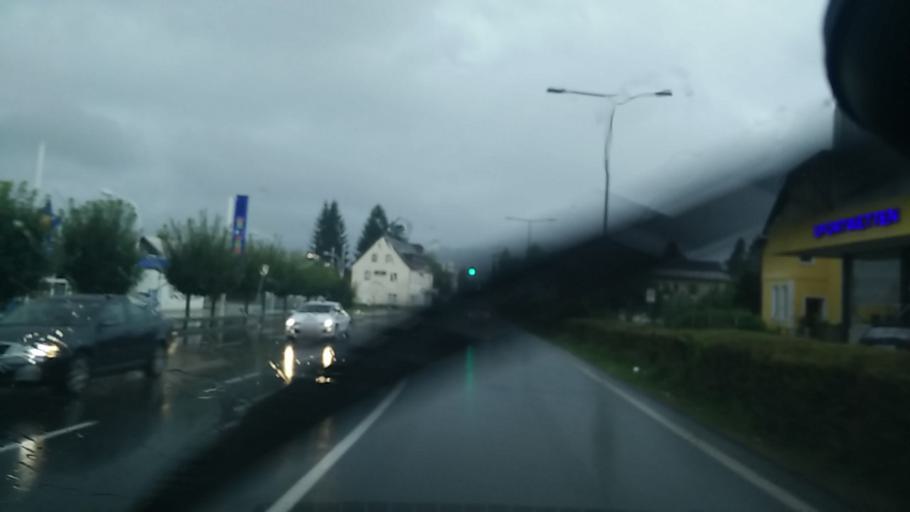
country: AT
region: Carinthia
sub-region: Villach Stadt
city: Villach
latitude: 46.5998
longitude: 13.8393
